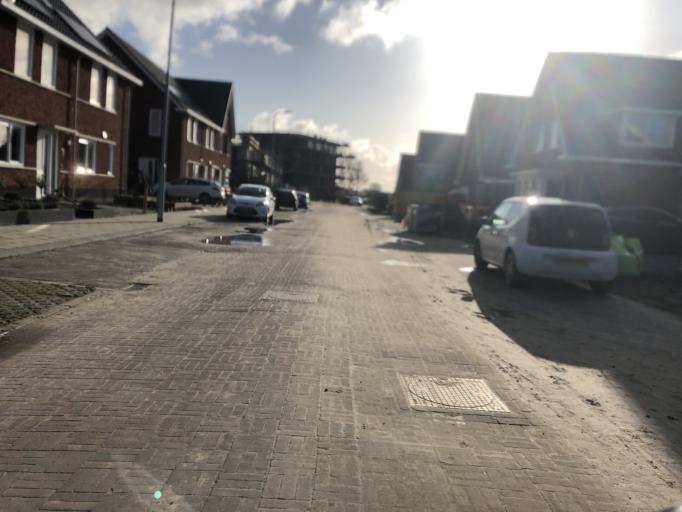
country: NL
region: Zeeland
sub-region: Gemeente Middelburg
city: Middelburg
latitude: 51.4843
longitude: 3.5949
